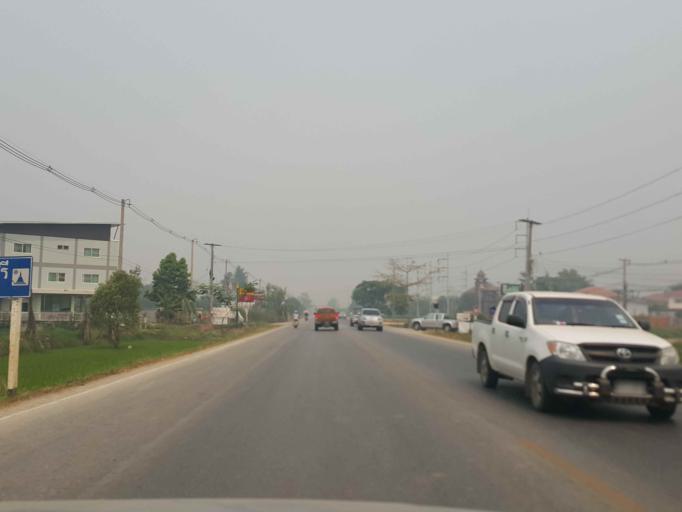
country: TH
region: Chiang Mai
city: San Sai
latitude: 18.8171
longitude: 99.0532
